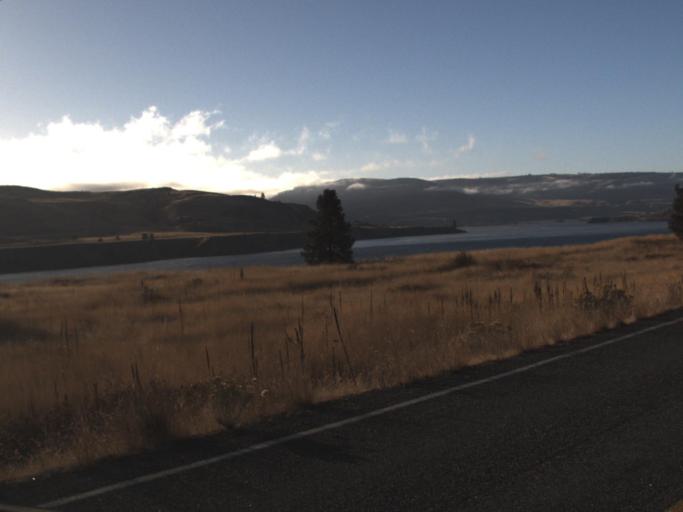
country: US
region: Washington
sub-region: Okanogan County
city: Coulee Dam
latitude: 47.9836
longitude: -118.6942
